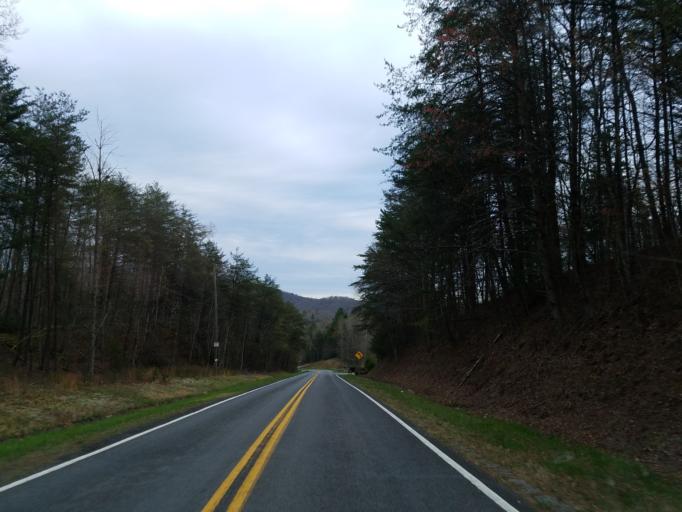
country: US
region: Georgia
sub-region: Fannin County
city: Blue Ridge
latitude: 34.6823
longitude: -84.2892
